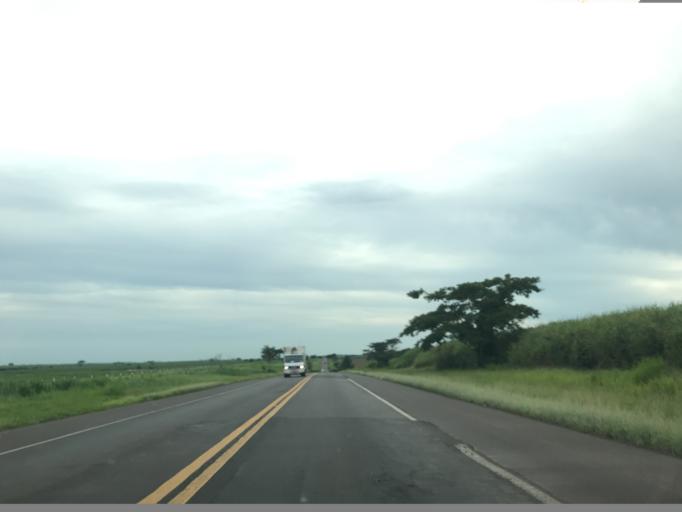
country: BR
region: Sao Paulo
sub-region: Tupa
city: Tupa
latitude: -21.6633
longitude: -50.5551
